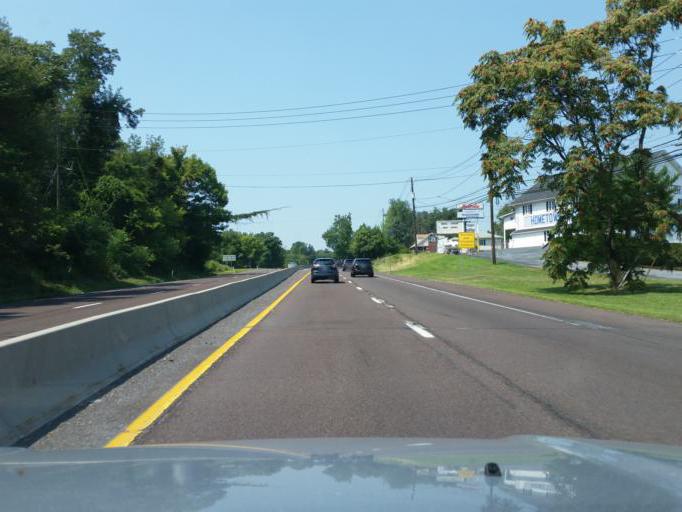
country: US
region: Pennsylvania
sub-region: Dauphin County
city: Hummelstown
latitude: 40.2610
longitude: -76.7300
